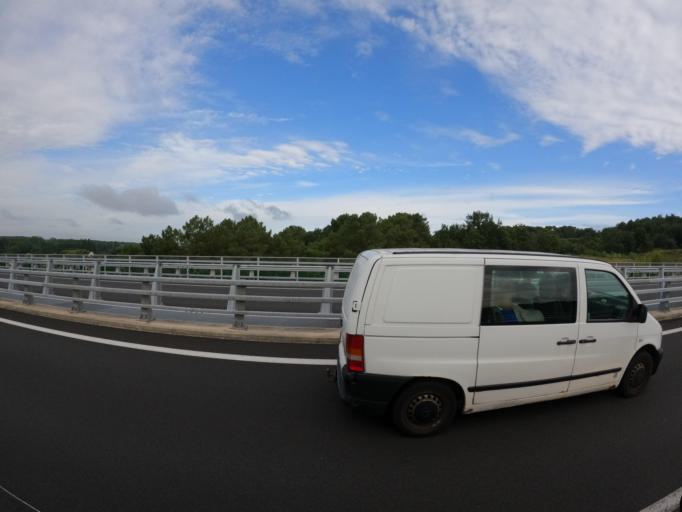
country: FR
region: Centre
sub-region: Departement d'Indre-et-Loire
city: Restigne
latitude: 47.2831
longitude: 0.2804
